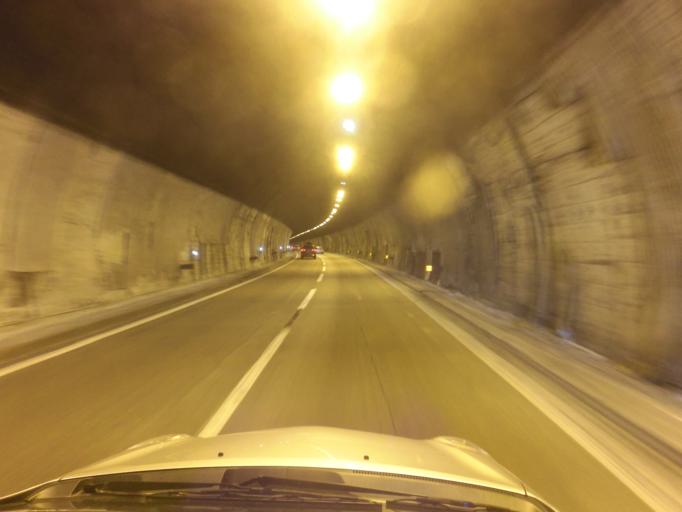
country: IT
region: Tuscany
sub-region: Province of Florence
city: Cavallina
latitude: 43.9470
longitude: 11.2139
